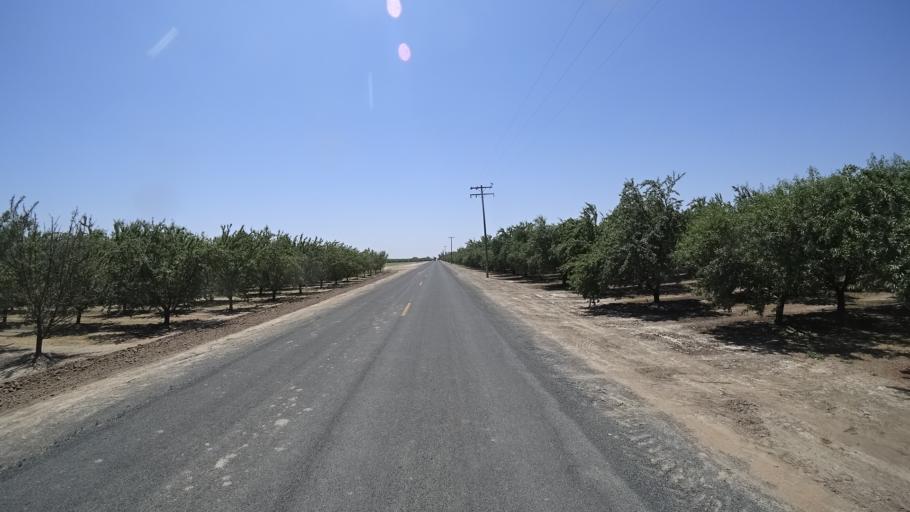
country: US
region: California
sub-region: Kings County
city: Armona
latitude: 36.2680
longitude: -119.7269
